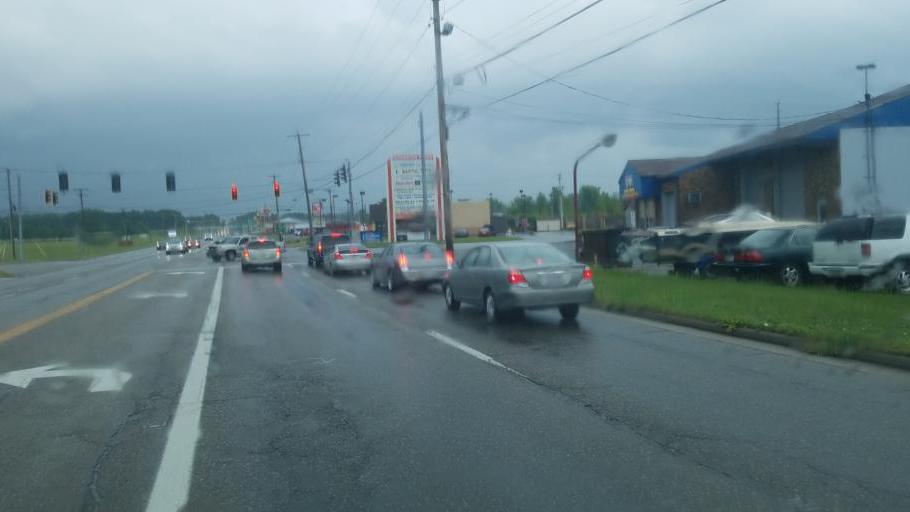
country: US
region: Ohio
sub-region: Trumbull County
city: Champion Heights
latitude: 41.2818
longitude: -80.8446
